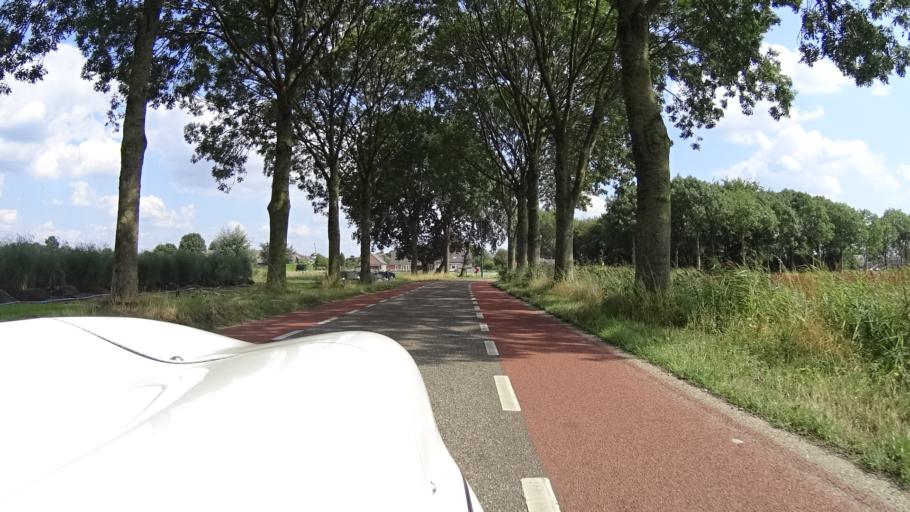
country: NL
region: North Brabant
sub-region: Gemeente Veghel
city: Veghel
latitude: 51.6521
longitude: 5.5427
